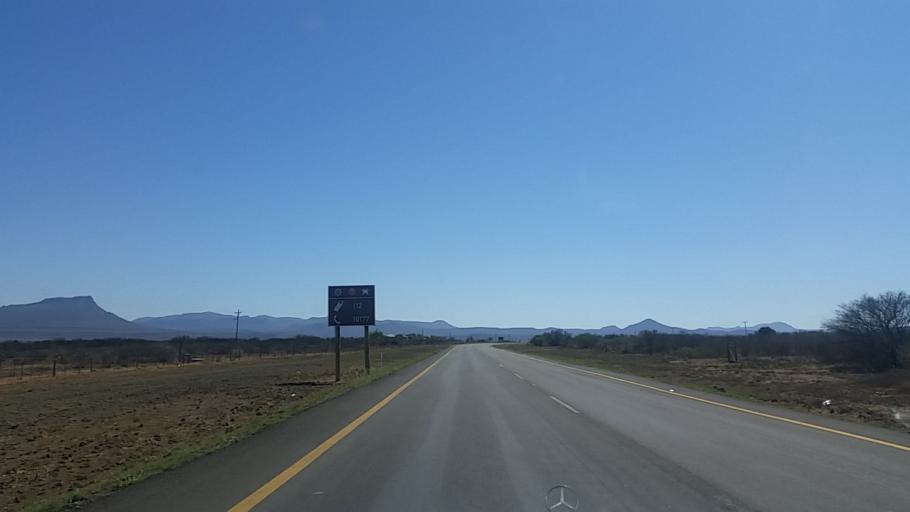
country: ZA
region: Eastern Cape
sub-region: Cacadu District Municipality
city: Graaff-Reinet
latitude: -32.2273
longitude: 24.5382
